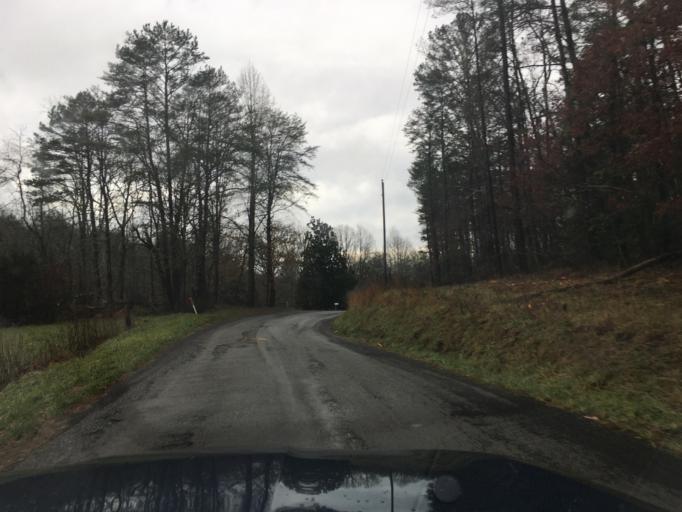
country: US
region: Georgia
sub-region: Fannin County
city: McCaysville
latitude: 35.1248
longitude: -84.3111
